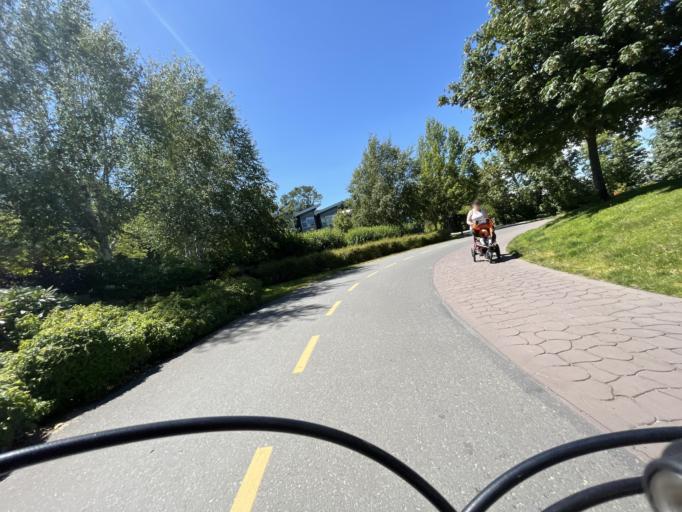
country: CA
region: British Columbia
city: Victoria
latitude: 48.4368
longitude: -123.3814
